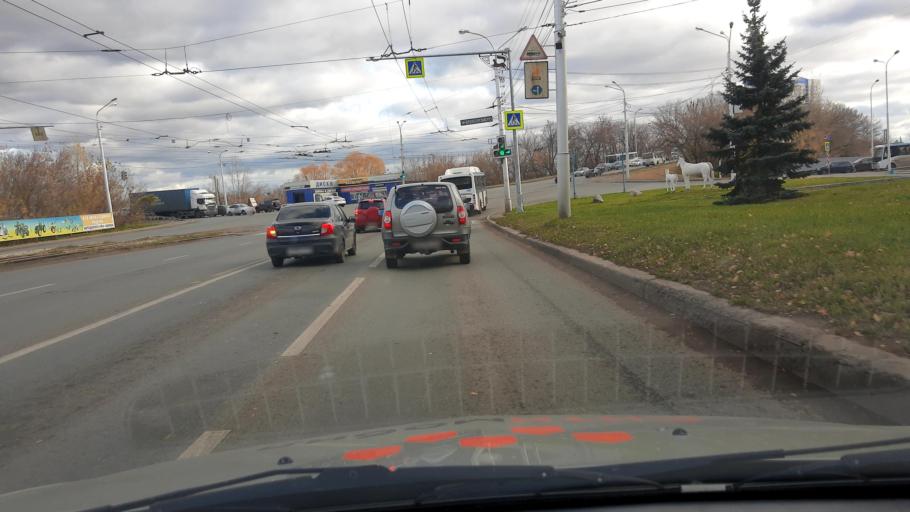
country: RU
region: Bashkortostan
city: Ufa
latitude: 54.8033
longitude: 56.1360
